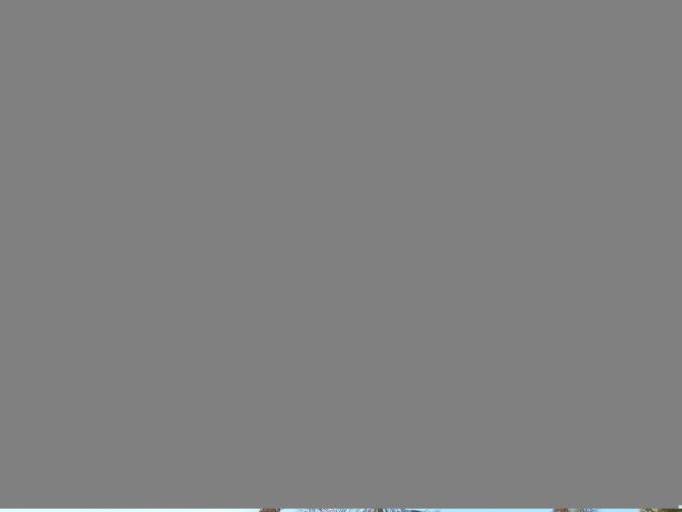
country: EG
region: Red Sea
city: Bur Safajah
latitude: 26.8461
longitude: 34.0003
